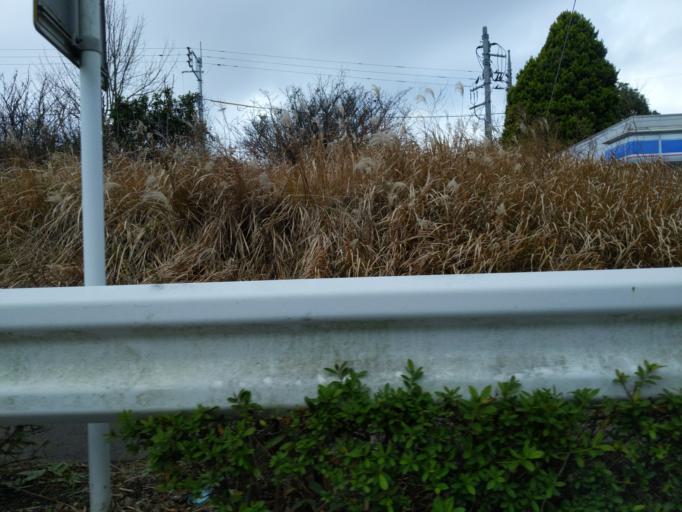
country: JP
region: Ibaraki
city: Ryugasaki
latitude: 35.9249
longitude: 140.2000
